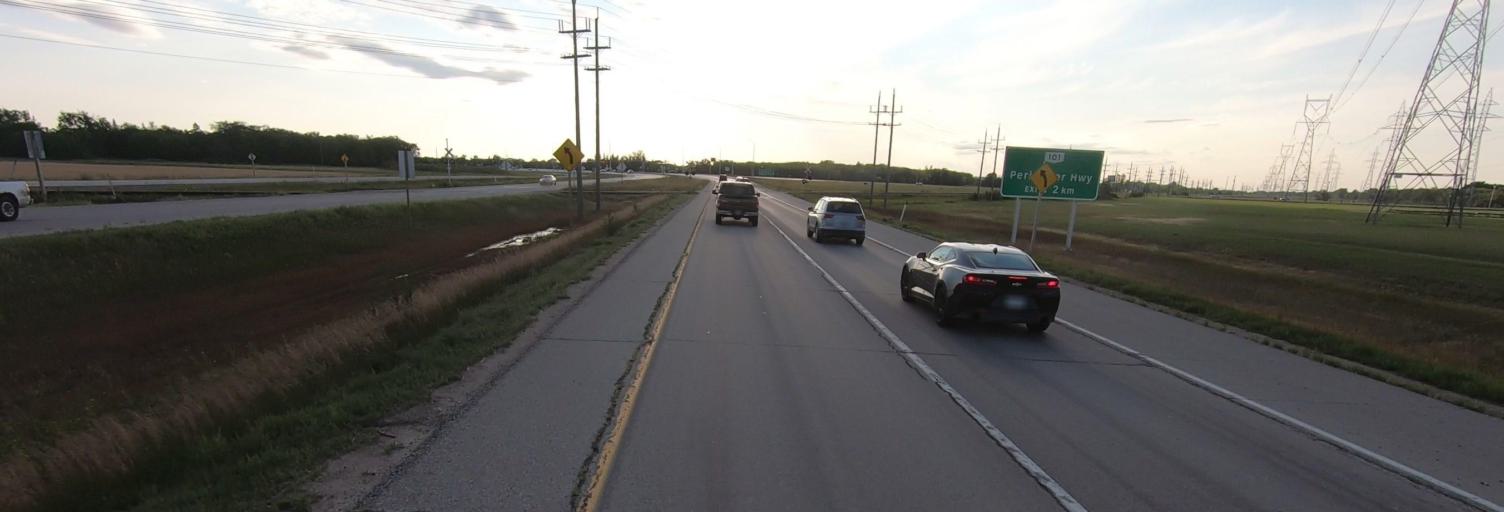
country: CA
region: Manitoba
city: Winnipeg
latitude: 49.9671
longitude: -97.0059
